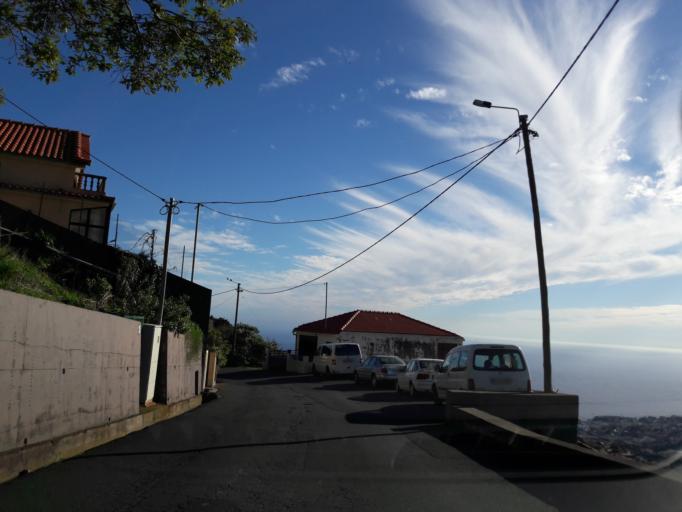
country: PT
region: Madeira
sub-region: Funchal
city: Nossa Senhora do Monte
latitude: 32.6772
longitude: -16.9116
